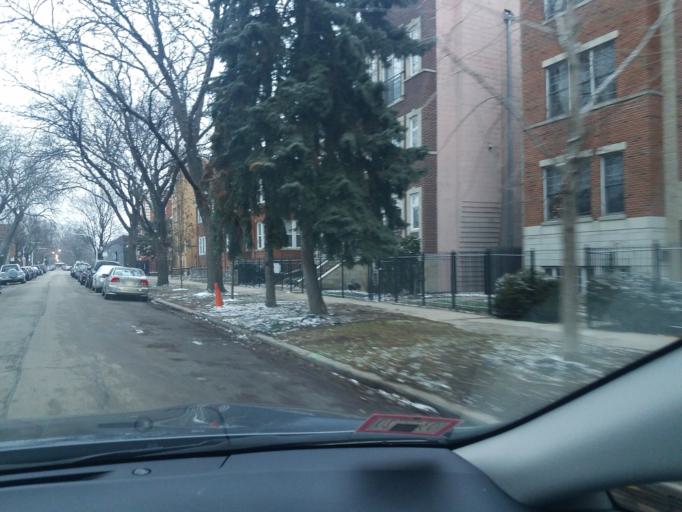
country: US
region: Illinois
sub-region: Cook County
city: Lincolnwood
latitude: 41.9598
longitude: -87.7021
